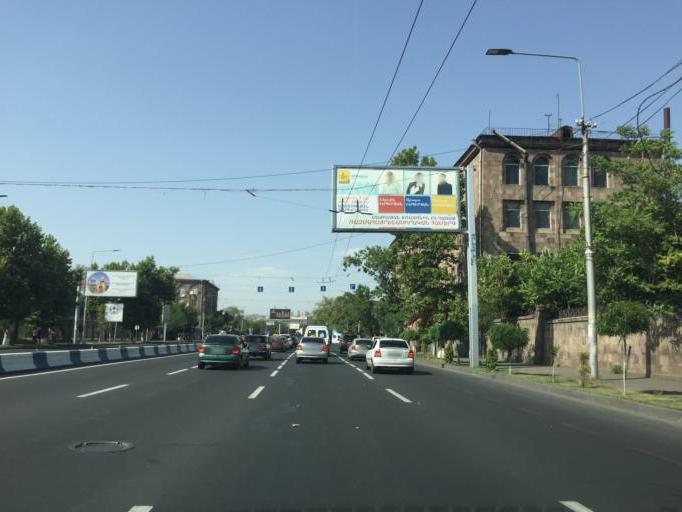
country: AM
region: Yerevan
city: Yerevan
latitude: 40.1622
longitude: 44.5039
